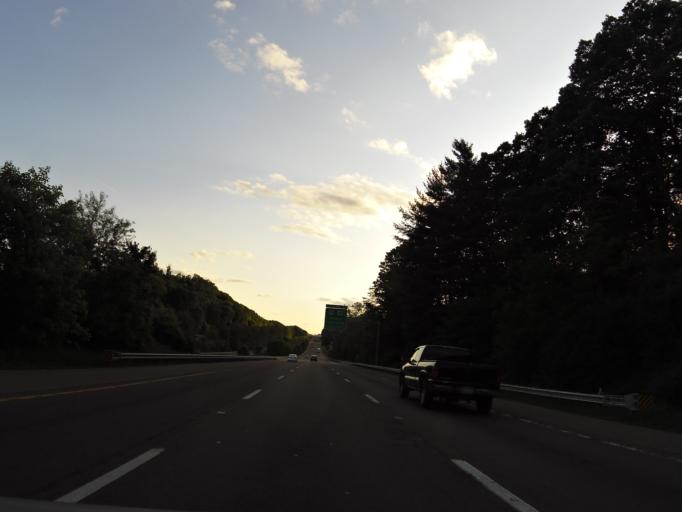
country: US
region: Virginia
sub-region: City of Bristol
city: Bristol
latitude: 36.6121
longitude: -82.2078
